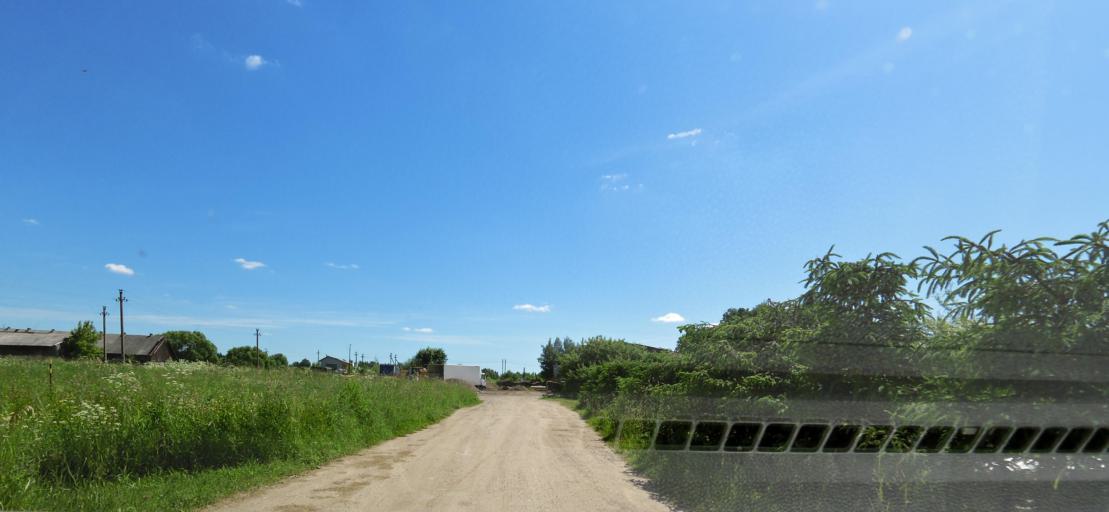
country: LT
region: Vilnius County
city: Pasilaiciai
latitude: 54.9848
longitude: 25.2302
